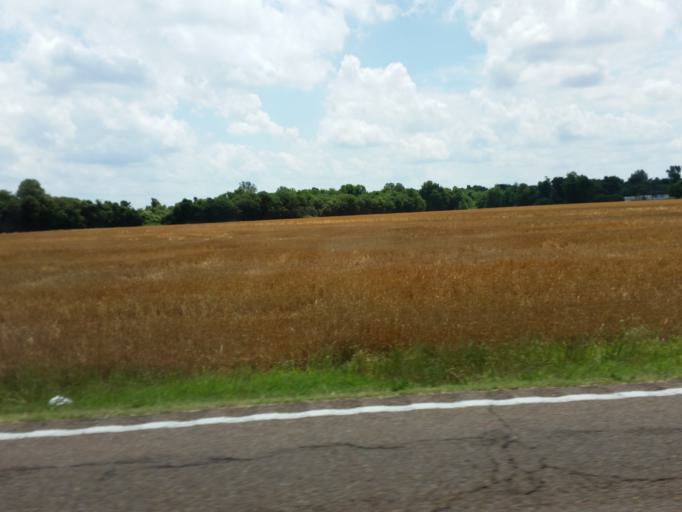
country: US
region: Tennessee
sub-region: Lake County
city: Tiptonville
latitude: 36.4040
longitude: -89.4508
